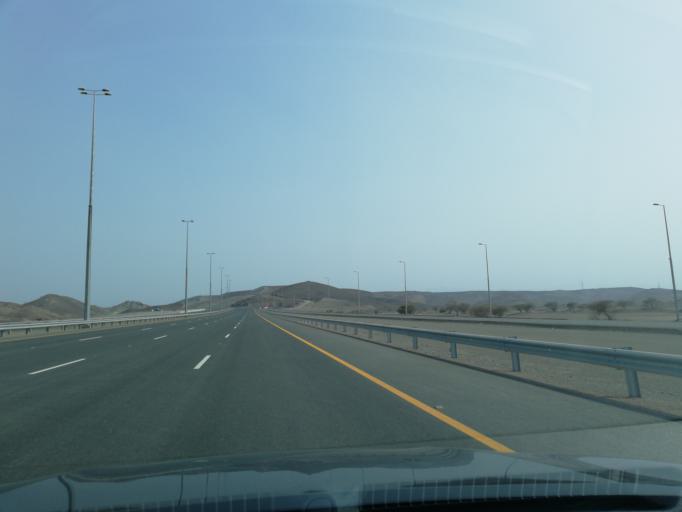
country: OM
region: Al Batinah
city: Al Liwa'
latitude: 24.3610
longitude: 56.5512
